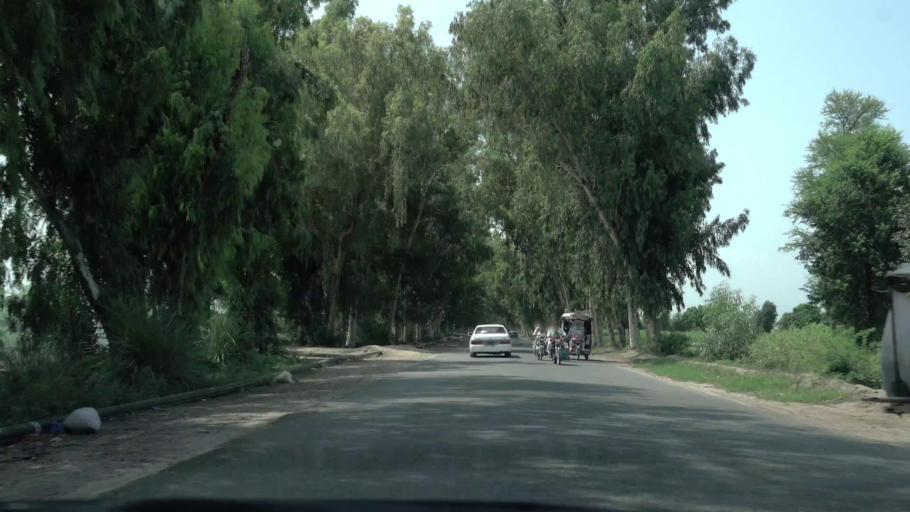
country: PK
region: Punjab
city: Gojra
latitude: 31.1718
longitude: 72.6197
